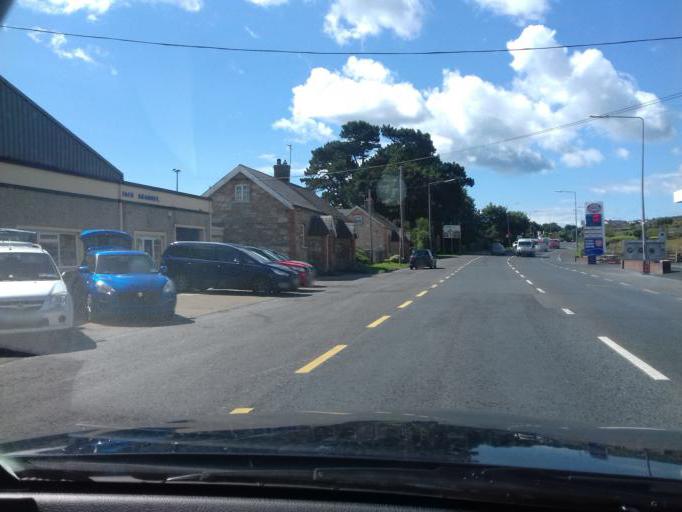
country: IE
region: Munster
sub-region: Waterford
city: Tra Mhor
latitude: 52.1707
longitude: -7.1416
